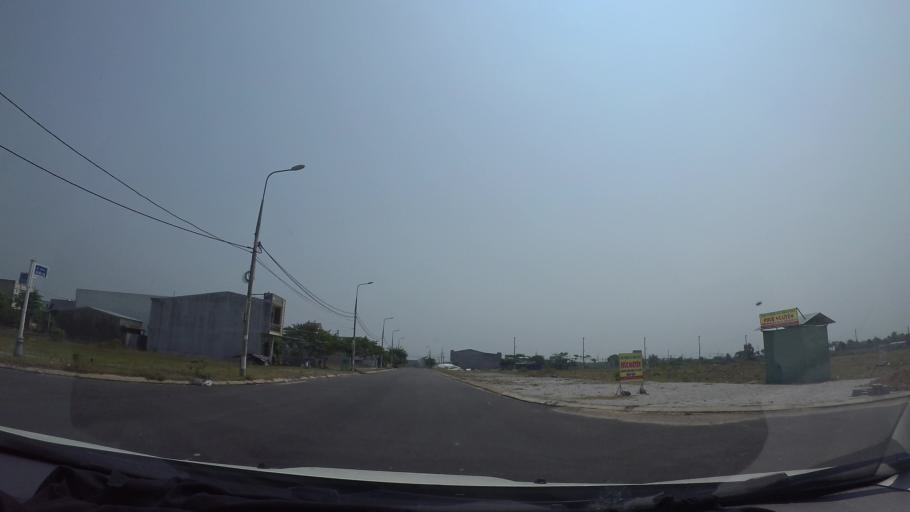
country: VN
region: Da Nang
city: Cam Le
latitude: 15.9763
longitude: 108.2117
